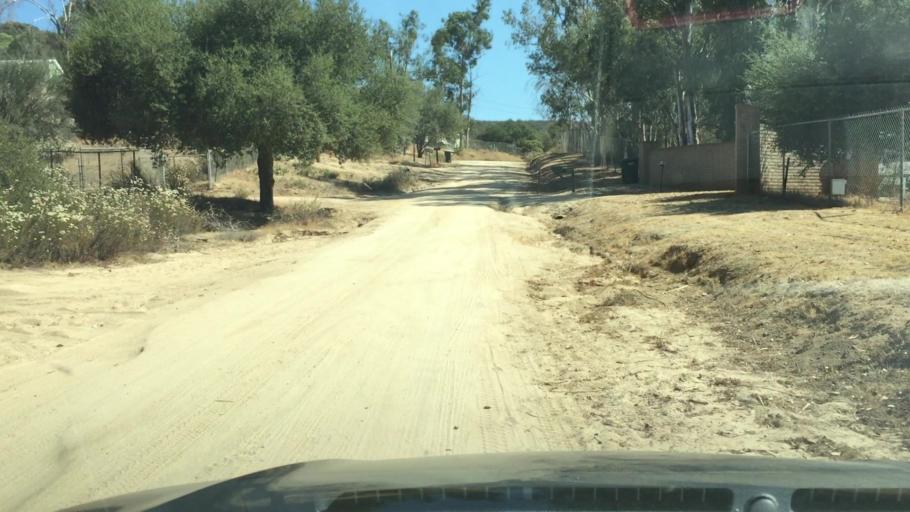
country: US
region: California
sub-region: San Diego County
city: Alpine
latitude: 32.7554
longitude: -116.7487
